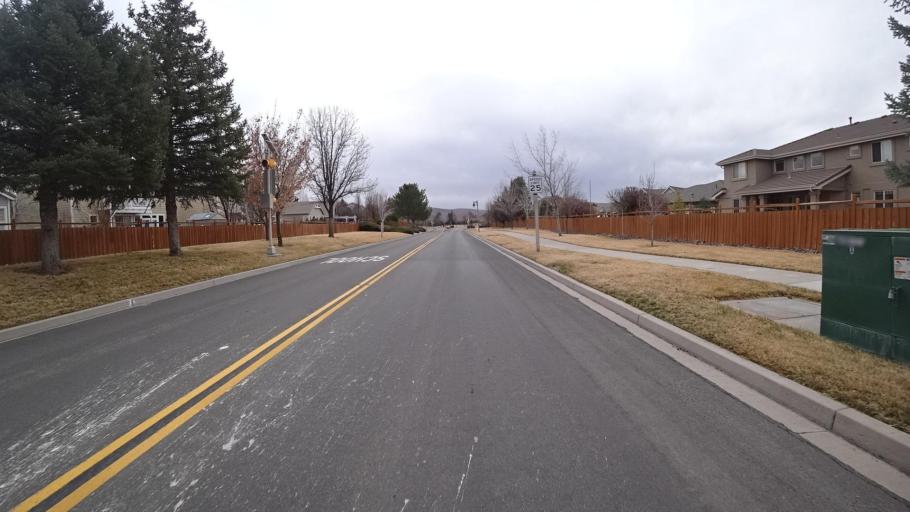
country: US
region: Nevada
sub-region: Washoe County
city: Spanish Springs
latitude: 39.6245
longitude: -119.6860
